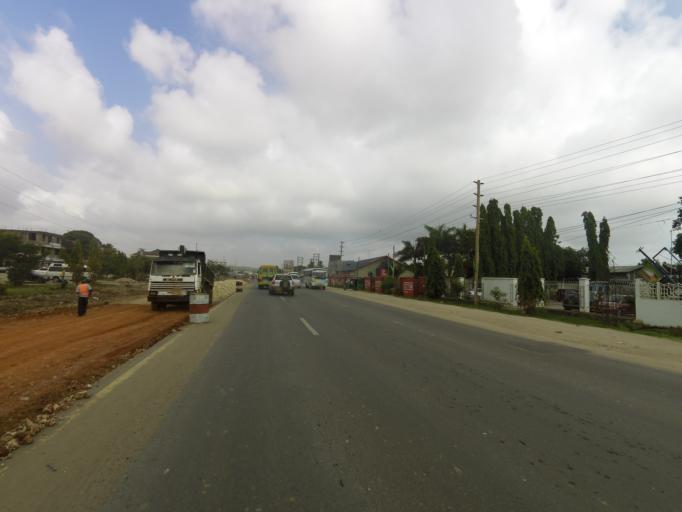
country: TZ
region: Dar es Salaam
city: Magomeni
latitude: -6.7682
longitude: 39.2342
